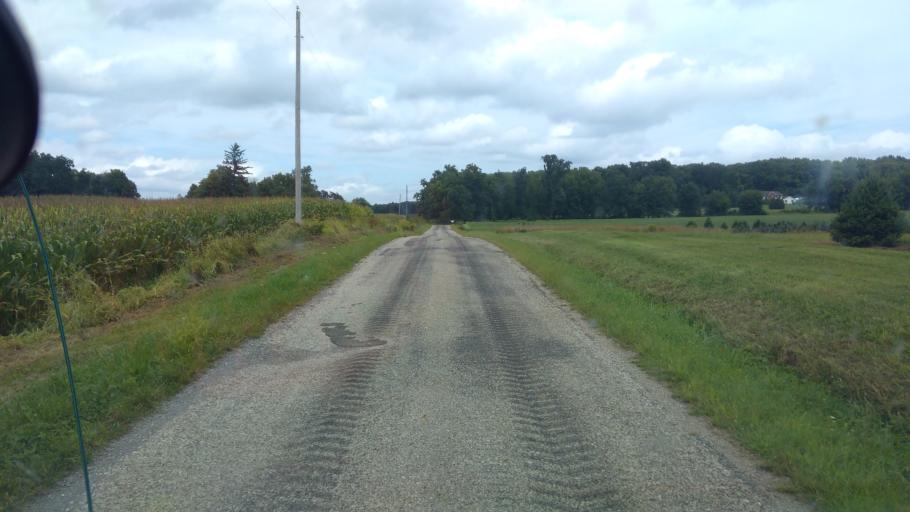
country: US
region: Ohio
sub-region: Richland County
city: Lincoln Heights
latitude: 40.8271
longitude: -82.4069
